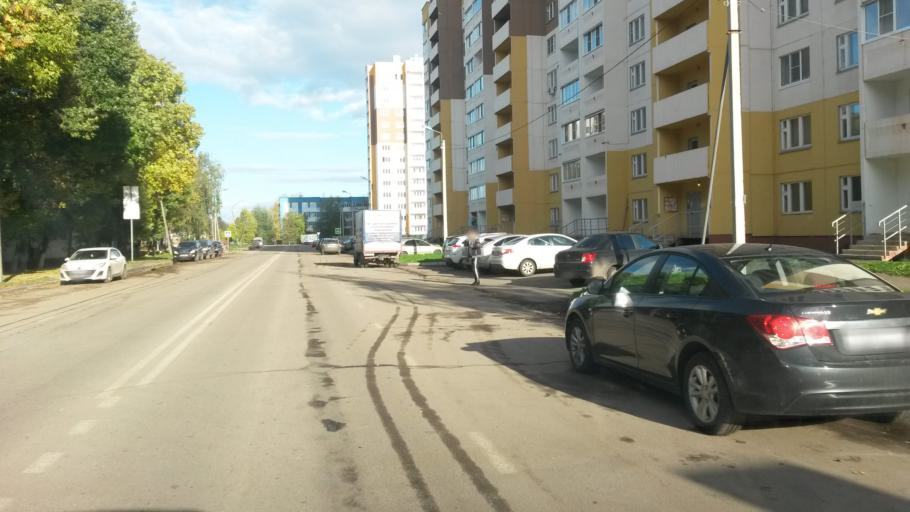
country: RU
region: Jaroslavl
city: Yaroslavl
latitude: 57.5692
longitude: 39.9307
